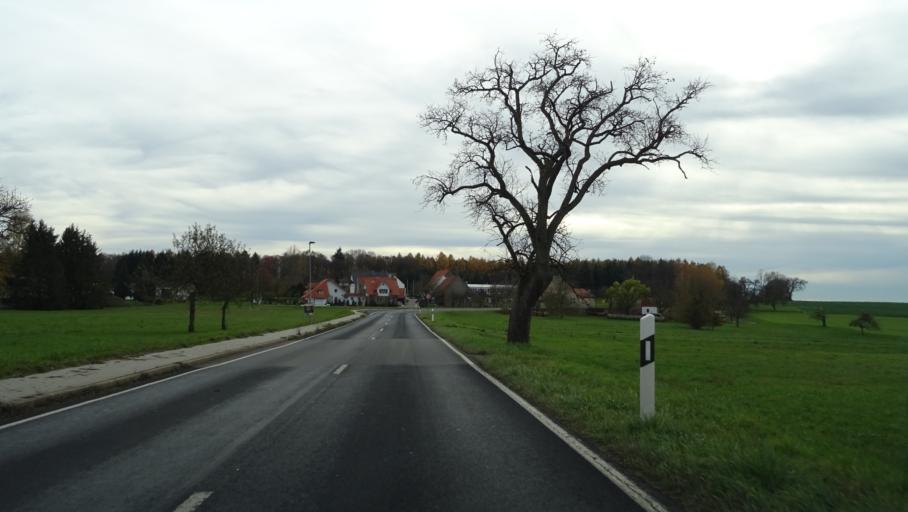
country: DE
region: Baden-Wuerttemberg
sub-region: Karlsruhe Region
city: Fahrenbach
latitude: 49.4084
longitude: 9.1580
